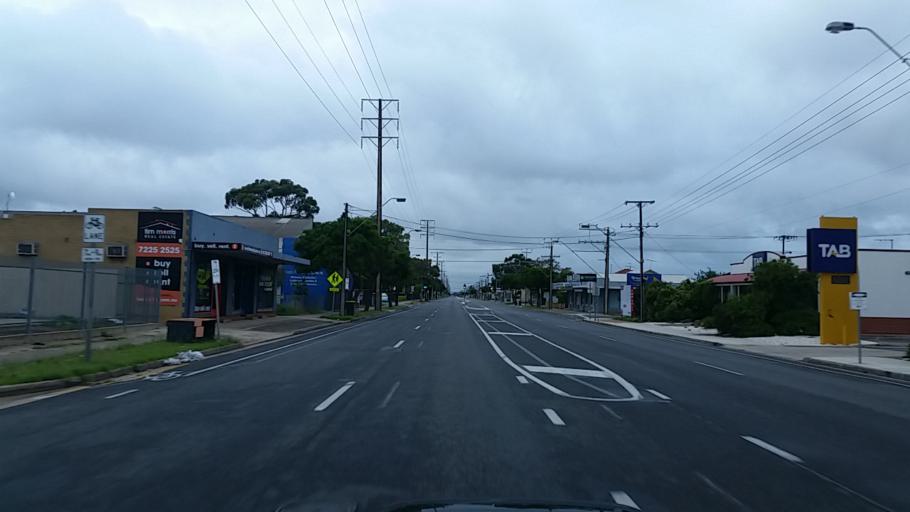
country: AU
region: South Australia
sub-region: Charles Sturt
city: Royal Park
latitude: -34.8714
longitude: 138.5123
